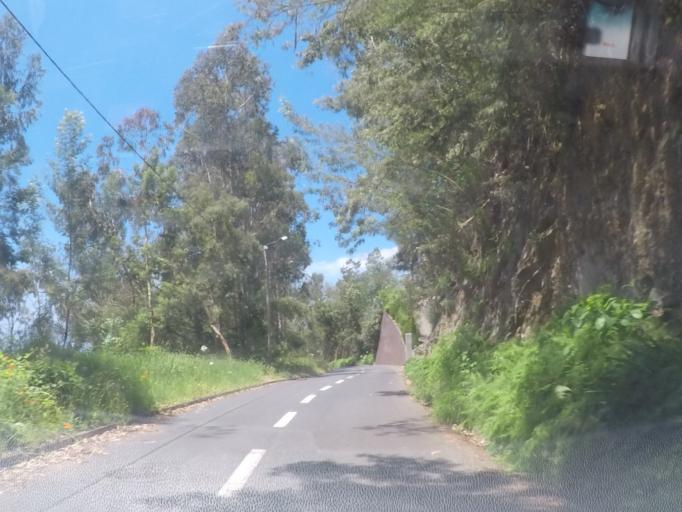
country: PT
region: Madeira
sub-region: Camara de Lobos
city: Curral das Freiras
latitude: 32.6881
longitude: -16.9770
